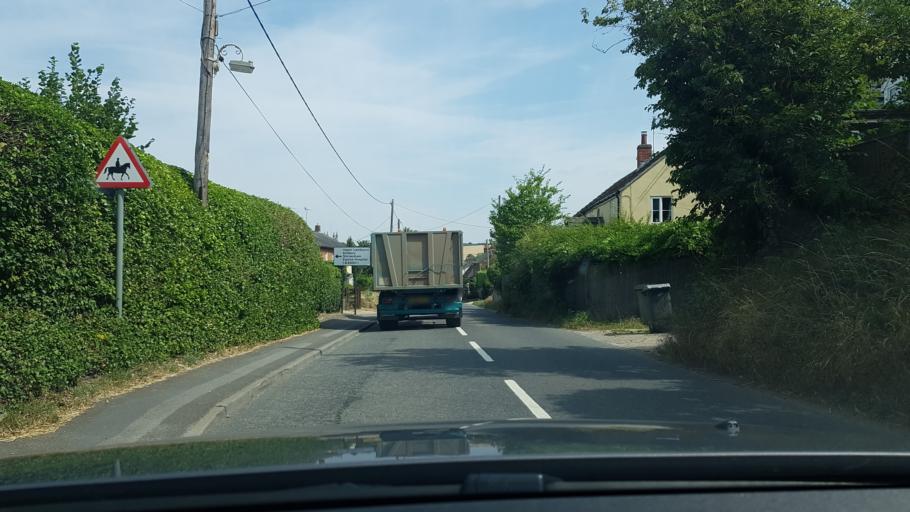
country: GB
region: England
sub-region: West Berkshire
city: Lambourn
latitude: 51.5051
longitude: -1.5345
